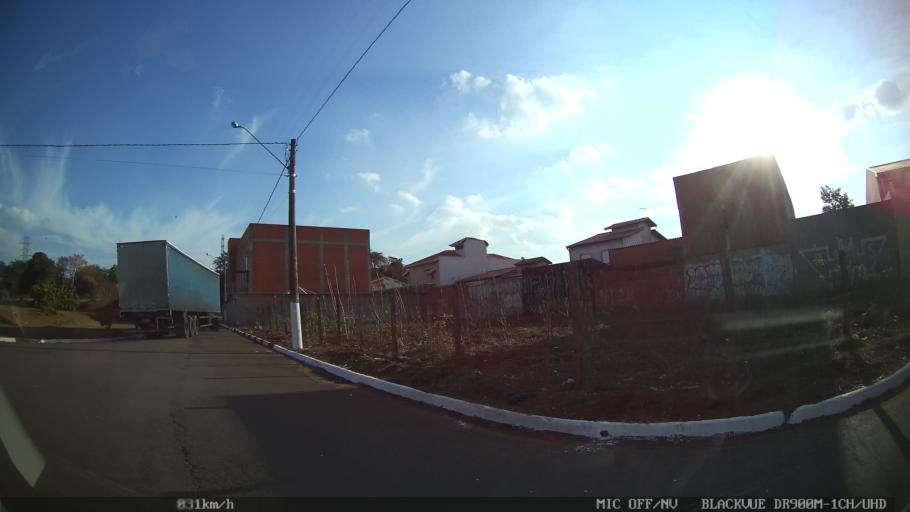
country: BR
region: Sao Paulo
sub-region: Hortolandia
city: Hortolandia
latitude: -22.8762
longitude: -47.1413
